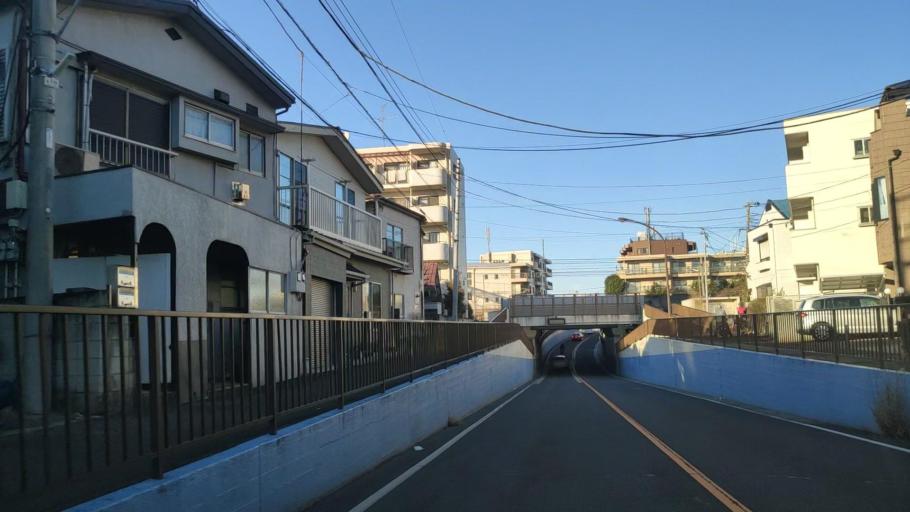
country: JP
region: Tokyo
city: Musashino
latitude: 35.7019
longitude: 139.5665
